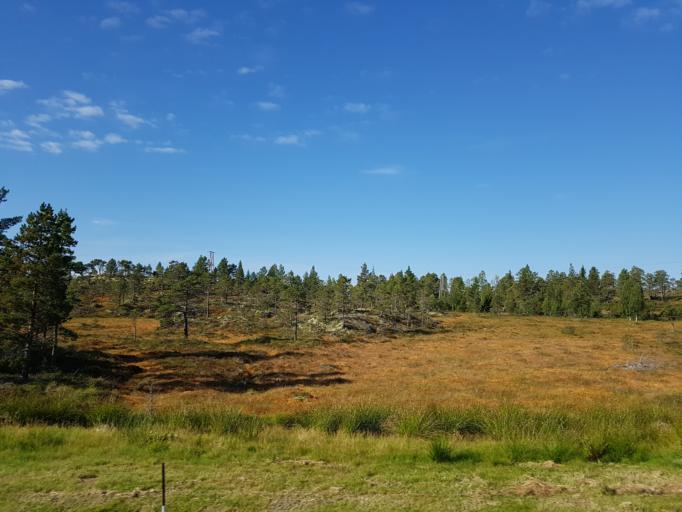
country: NO
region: Sor-Trondelag
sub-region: Trondheim
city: Trondheim
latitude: 63.6390
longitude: 10.2715
